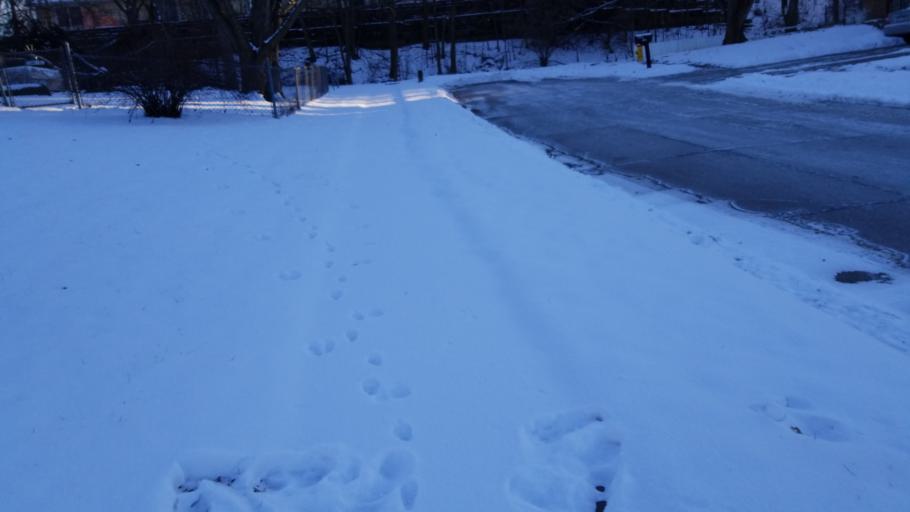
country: US
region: Nebraska
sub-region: Sarpy County
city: Offutt Air Force Base
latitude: 41.1331
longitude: -95.9585
